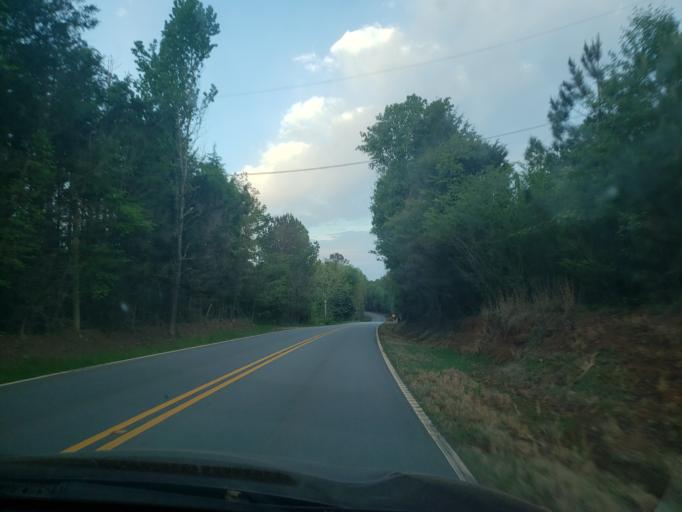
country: US
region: Alabama
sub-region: Tallapoosa County
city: Camp Hill
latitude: 32.6986
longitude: -85.7216
